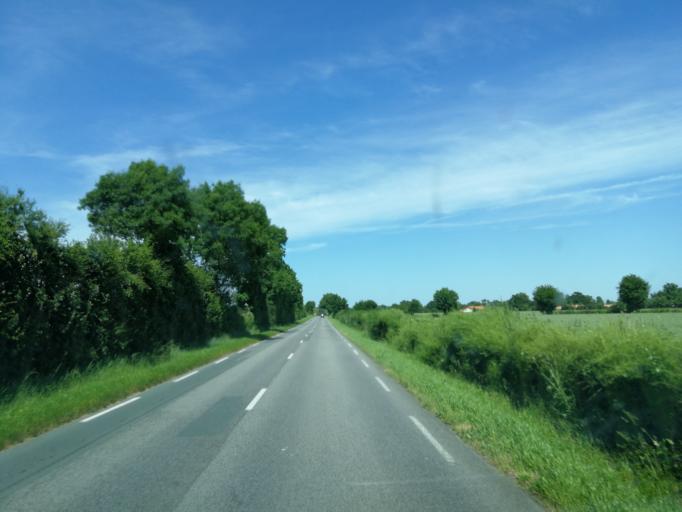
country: FR
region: Poitou-Charentes
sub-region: Departement des Deux-Sevres
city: Saint-Varent
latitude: 46.8954
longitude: -0.2965
